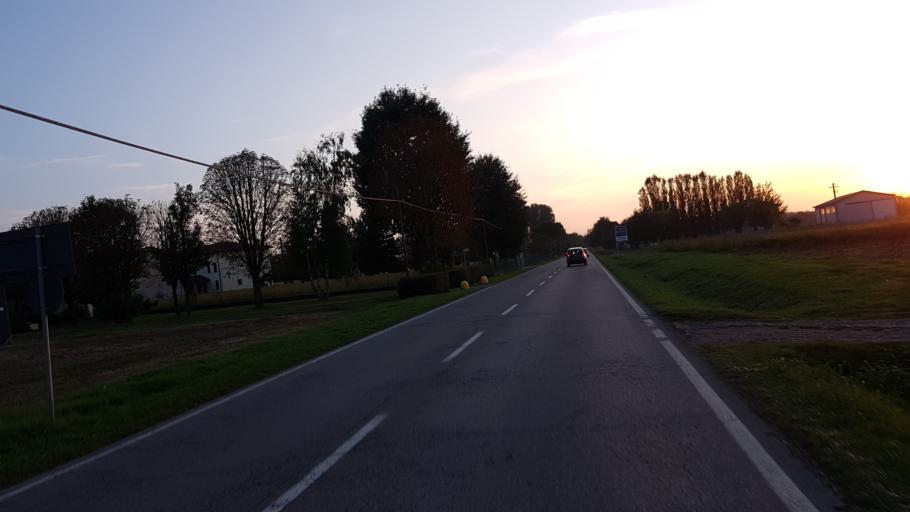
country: IT
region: Emilia-Romagna
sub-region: Provincia di Modena
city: Camposanto
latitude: 44.7900
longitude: 11.1584
